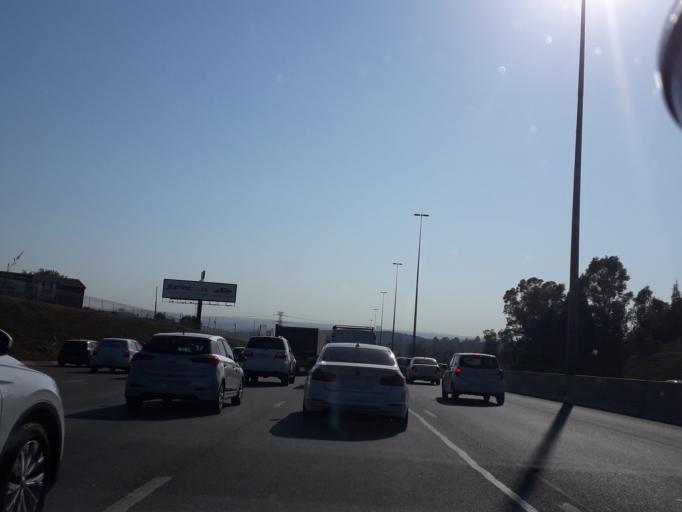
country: ZA
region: Gauteng
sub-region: City of Johannesburg Metropolitan Municipality
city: Diepsloot
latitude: -26.0367
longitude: 28.0194
